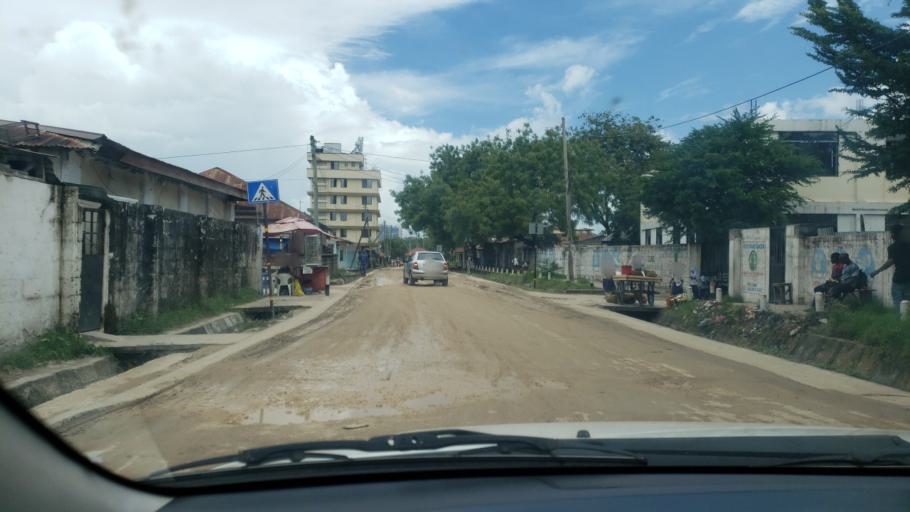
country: TZ
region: Dar es Salaam
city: Magomeni
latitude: -6.8111
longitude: 39.2578
